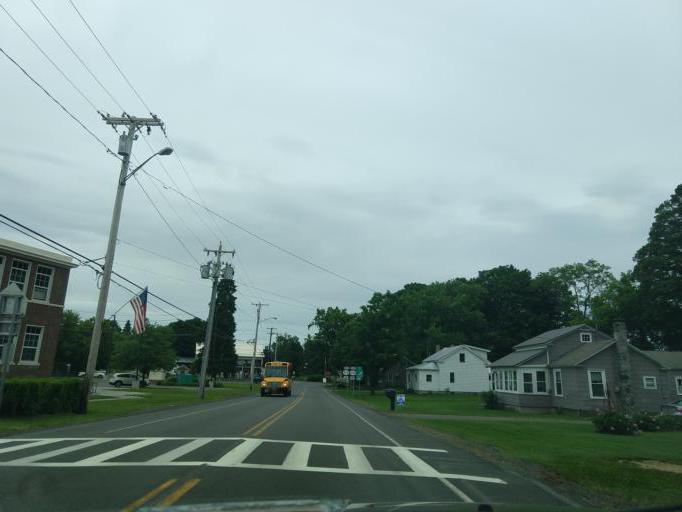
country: US
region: New York
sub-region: Cortland County
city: Munsons Corners
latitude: 42.5094
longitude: -76.1951
